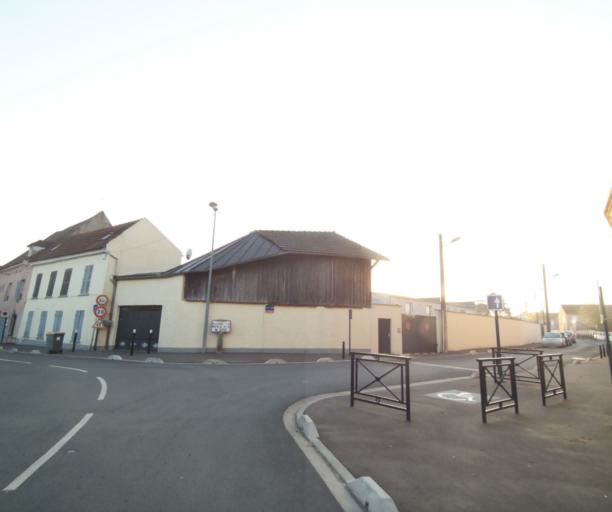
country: FR
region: Ile-de-France
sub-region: Departement du Val-d'Oise
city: Gonesse
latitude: 48.9827
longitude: 2.4464
